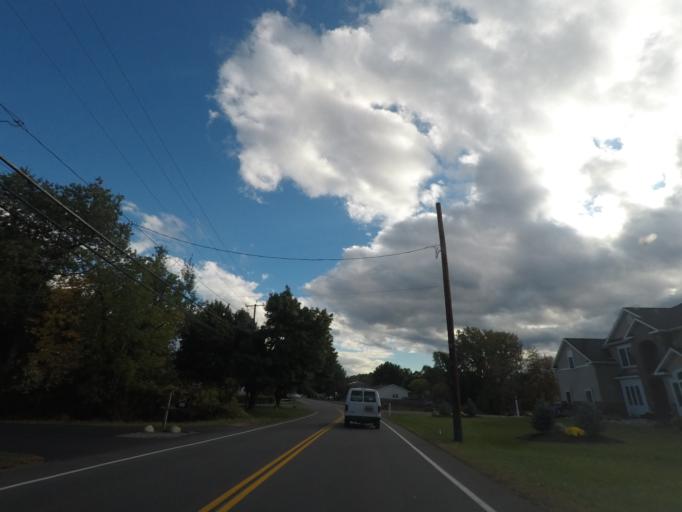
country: US
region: New York
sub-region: Schenectady County
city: Niskayuna
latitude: 42.7511
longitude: -73.8388
